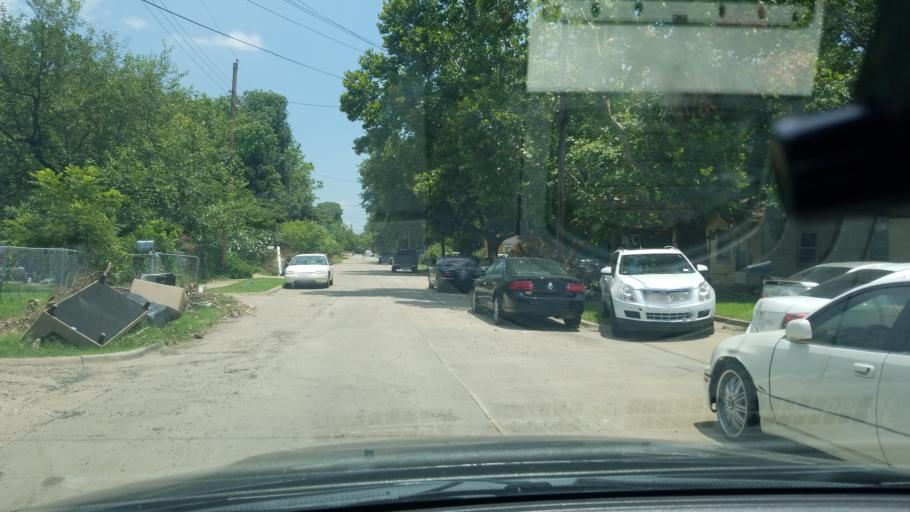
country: US
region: Texas
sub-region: Dallas County
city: Balch Springs
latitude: 32.7312
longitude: -96.6700
